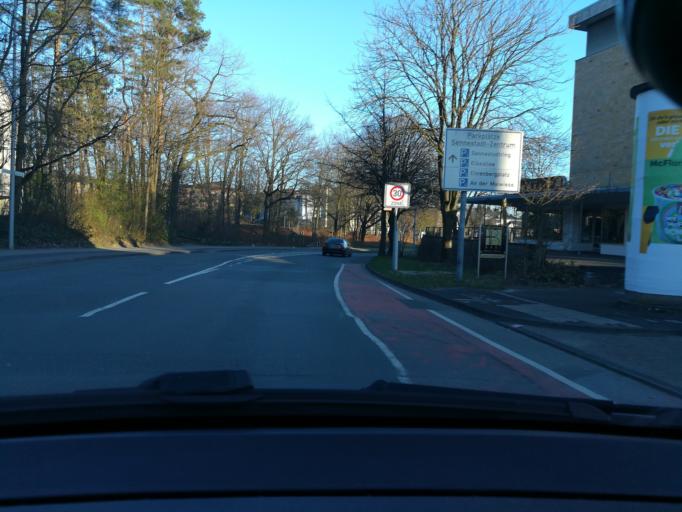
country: DE
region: North Rhine-Westphalia
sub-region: Regierungsbezirk Detmold
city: Oerlinghausen
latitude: 51.9475
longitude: 8.5825
